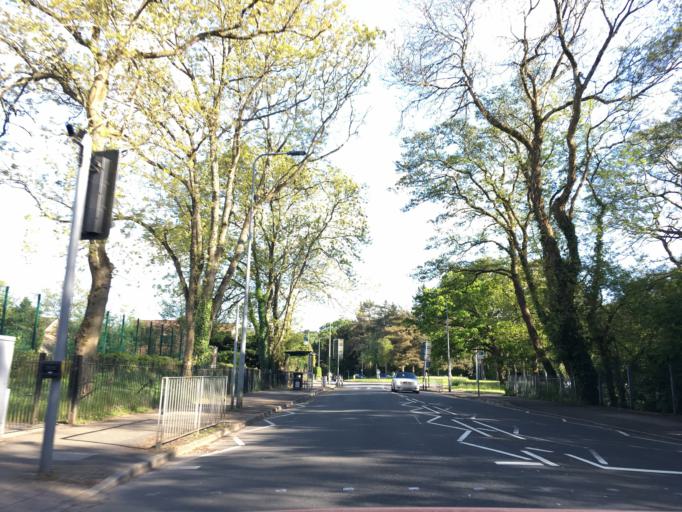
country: GB
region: Wales
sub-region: Cardiff
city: Cardiff
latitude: 51.5172
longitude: -3.1766
